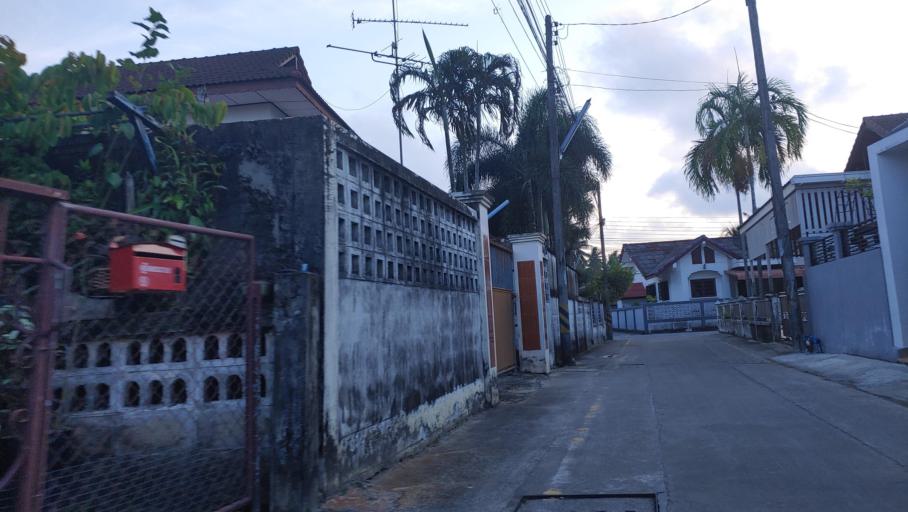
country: TH
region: Narathiwat
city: Narathiwat
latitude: 6.4391
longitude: 101.8173
